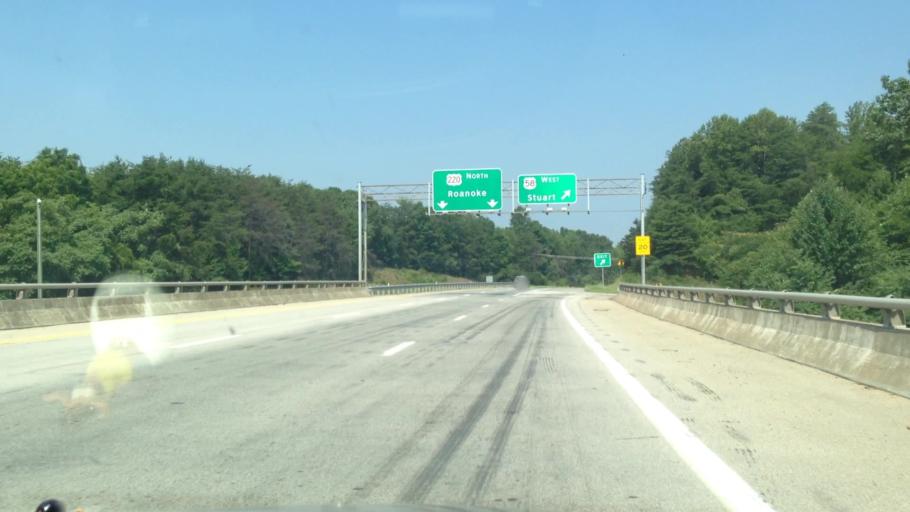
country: US
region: Virginia
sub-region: Henry County
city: Horse Pasture
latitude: 36.6485
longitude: -79.9149
